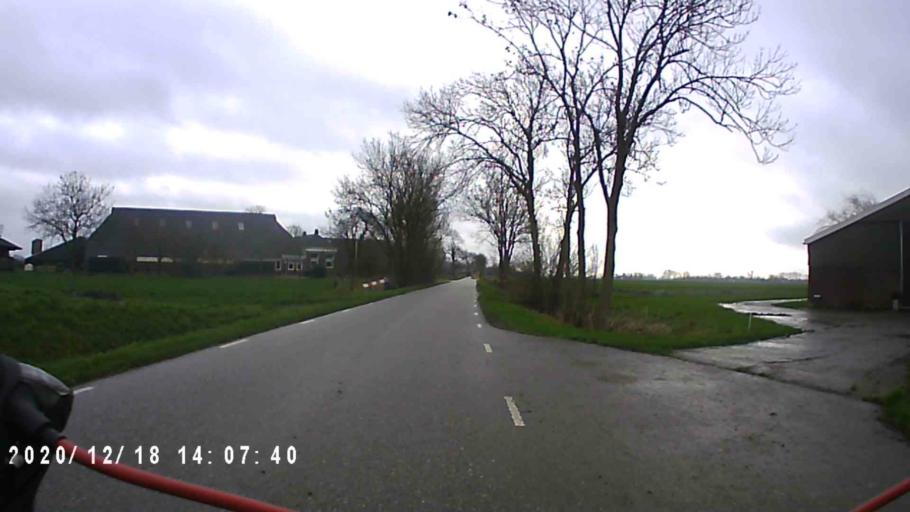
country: NL
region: Groningen
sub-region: Gemeente Bedum
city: Bedum
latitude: 53.2840
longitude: 6.6560
